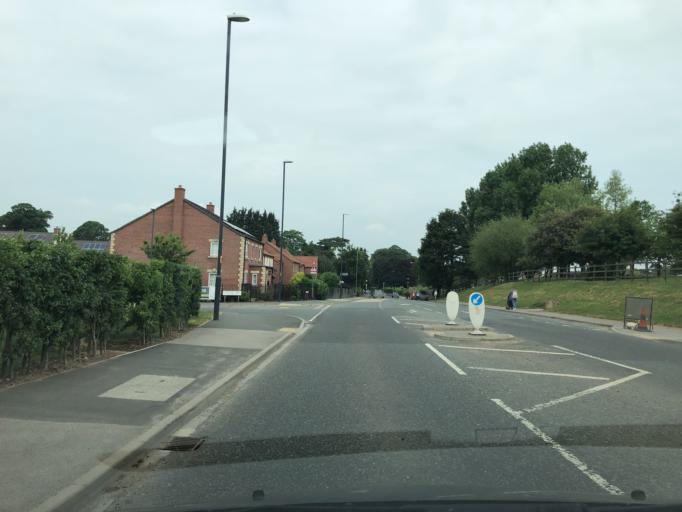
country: GB
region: England
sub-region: North Yorkshire
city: Boroughbridge
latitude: 54.0886
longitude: -1.3971
